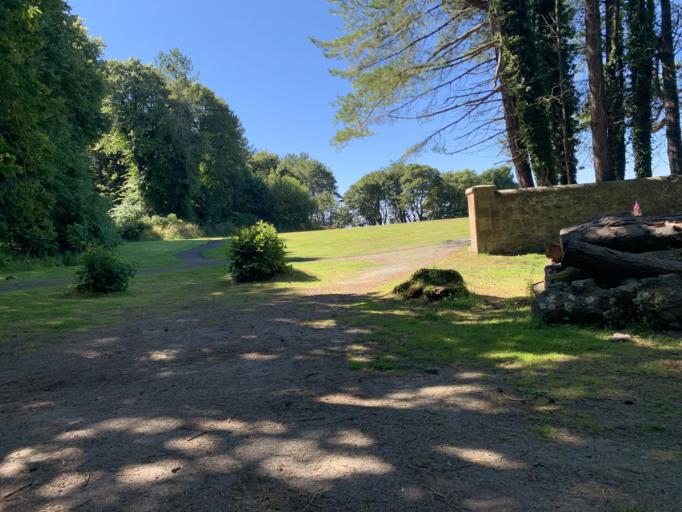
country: GB
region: Scotland
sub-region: South Ayrshire
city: Maybole
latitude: 55.3535
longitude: -4.7899
